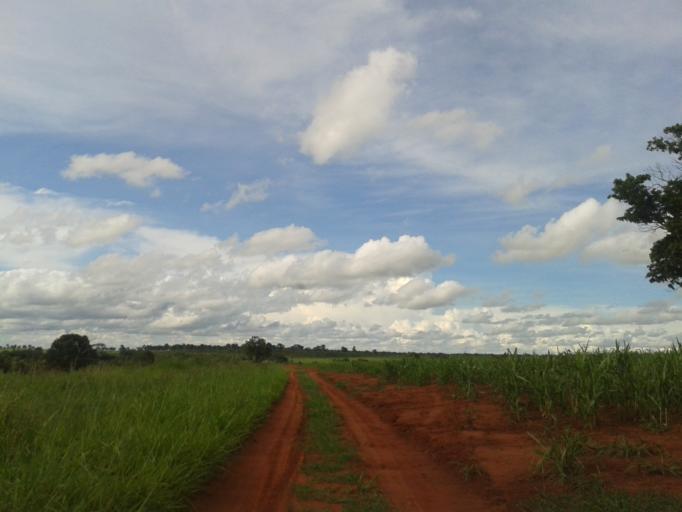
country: BR
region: Minas Gerais
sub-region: Santa Vitoria
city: Santa Vitoria
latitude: -19.1407
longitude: -50.4866
